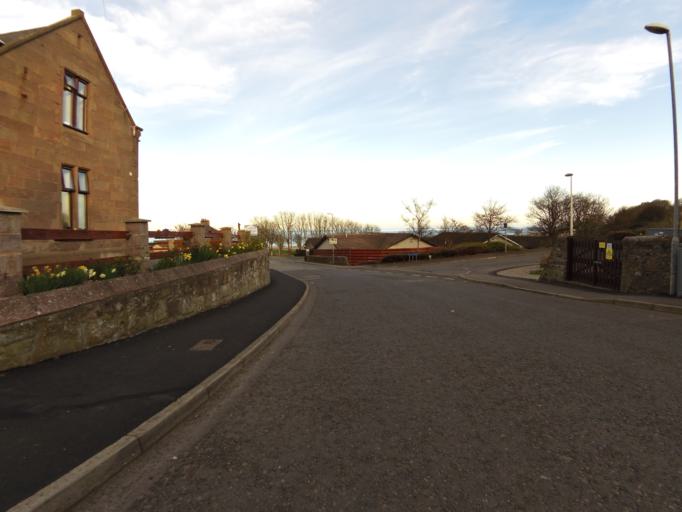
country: GB
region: Scotland
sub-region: Aberdeenshire
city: Inverbervie
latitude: 56.8433
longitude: -2.2779
